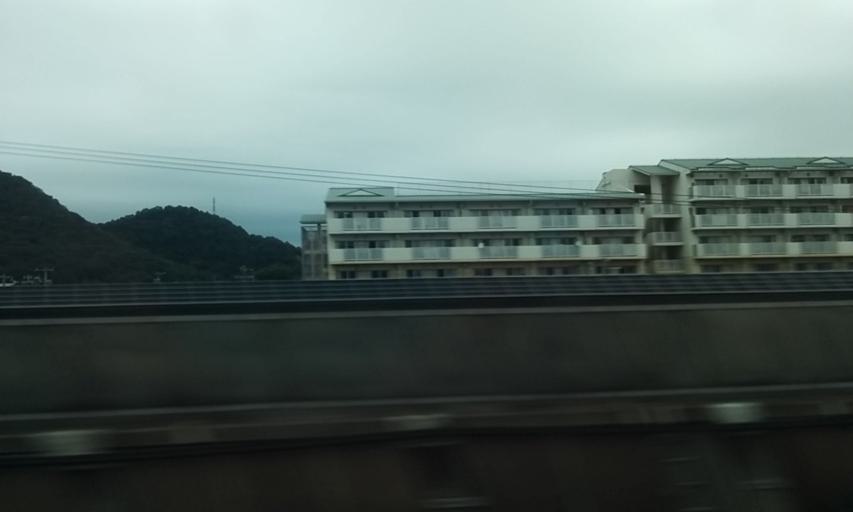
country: JP
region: Hyogo
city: Himeji
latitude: 34.8310
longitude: 134.6388
